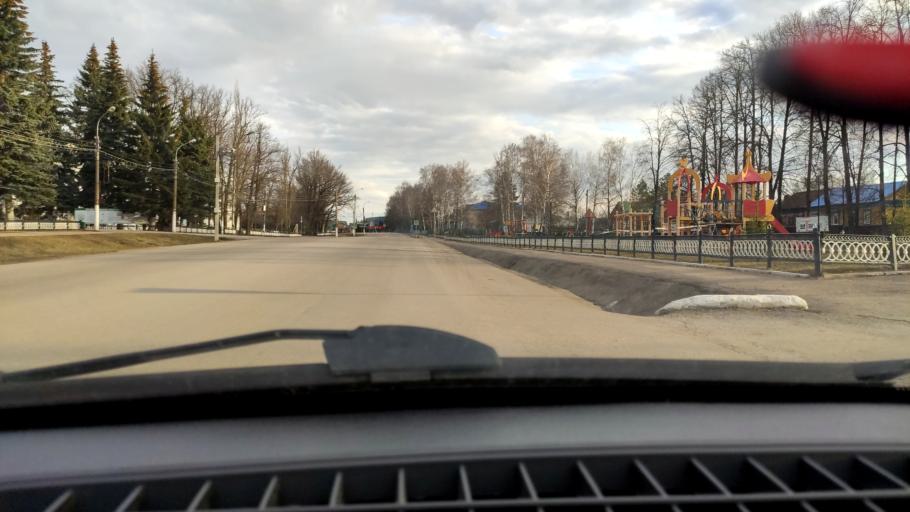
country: RU
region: Bashkortostan
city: Tolbazy
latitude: 54.0141
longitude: 55.8863
